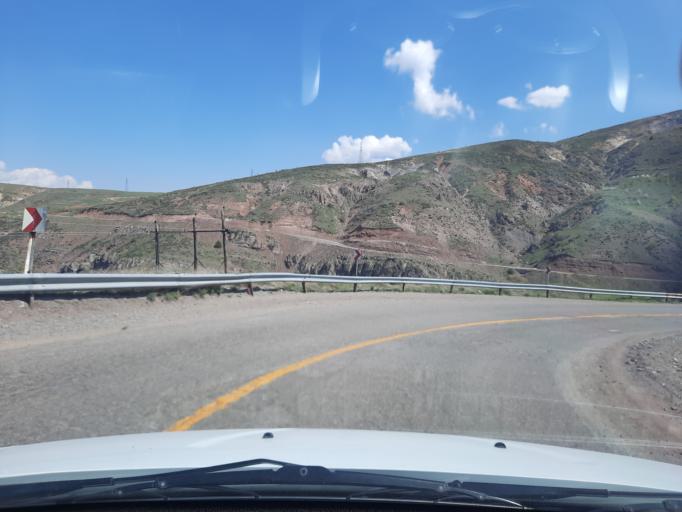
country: IR
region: Qazvin
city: Qazvin
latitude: 36.4072
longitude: 50.2259
